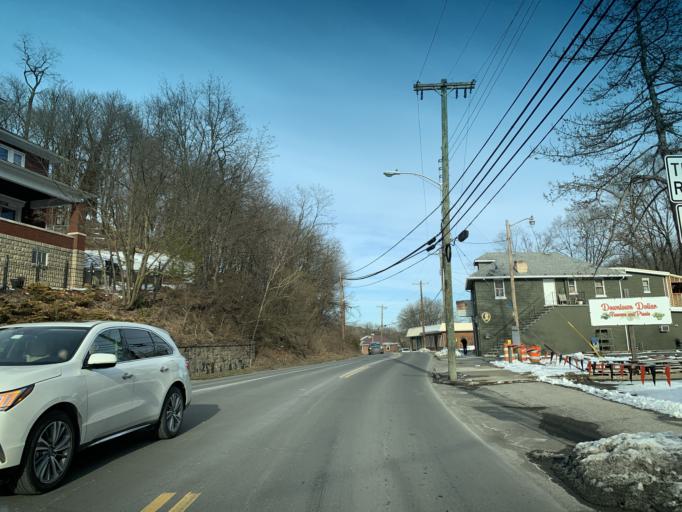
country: US
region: Maryland
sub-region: Allegany County
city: Cumberland
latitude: 39.6493
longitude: -78.7838
